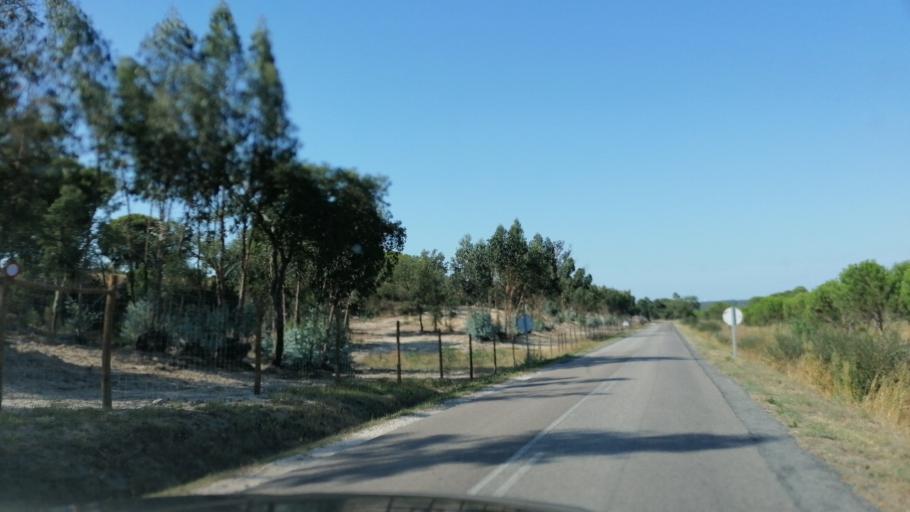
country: PT
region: Evora
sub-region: Vendas Novas
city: Vendas Novas
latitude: 38.7848
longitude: -8.5839
